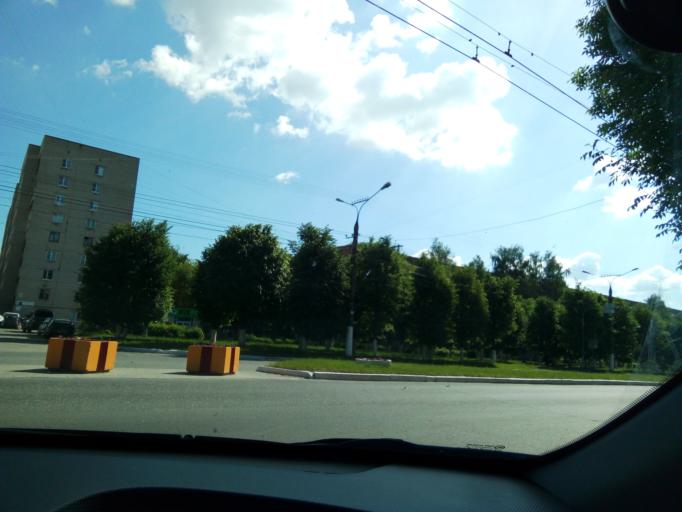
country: RU
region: Chuvashia
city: Novocheboksarsk
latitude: 56.1158
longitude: 47.4832
